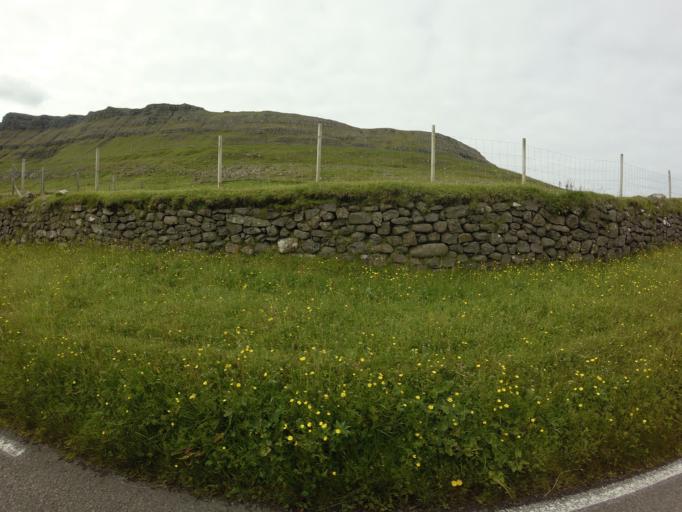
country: FO
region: Suduroy
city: Tvoroyri
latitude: 61.5925
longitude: -6.9428
